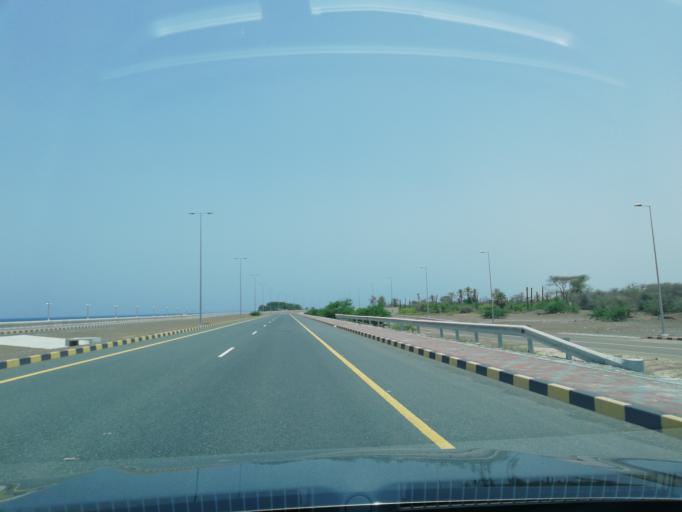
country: OM
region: Al Batinah
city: Shinas
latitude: 24.8311
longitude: 56.4317
